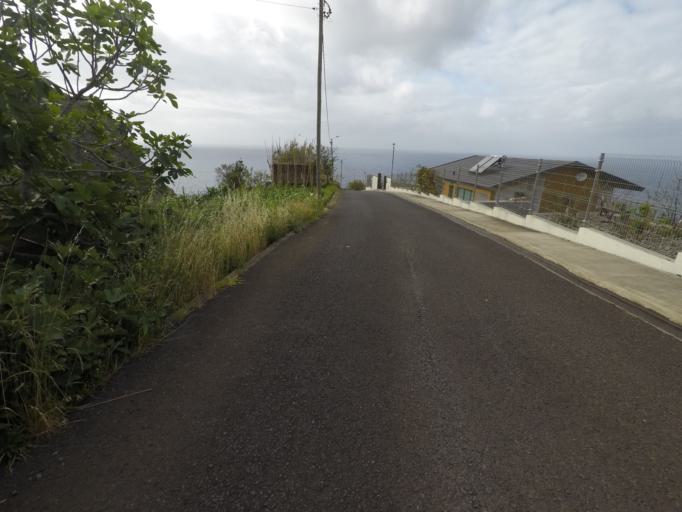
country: PT
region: Madeira
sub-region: Sao Vicente
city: Sao Vicente
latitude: 32.8265
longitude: -16.9741
